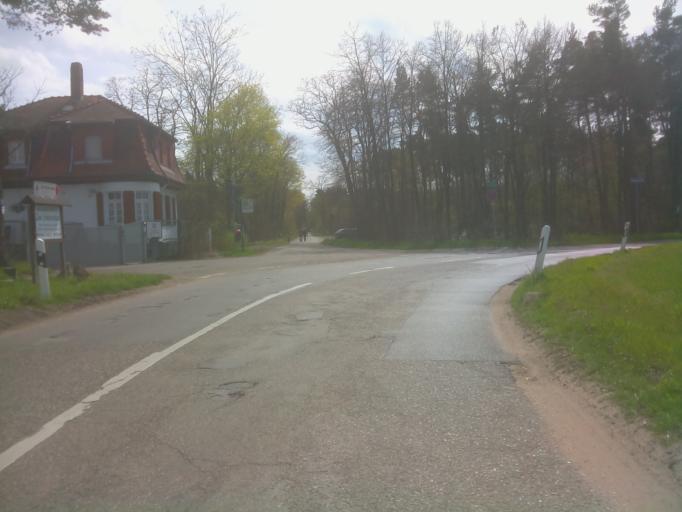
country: DE
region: Hesse
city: Lampertheim
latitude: 49.5664
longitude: 8.4932
